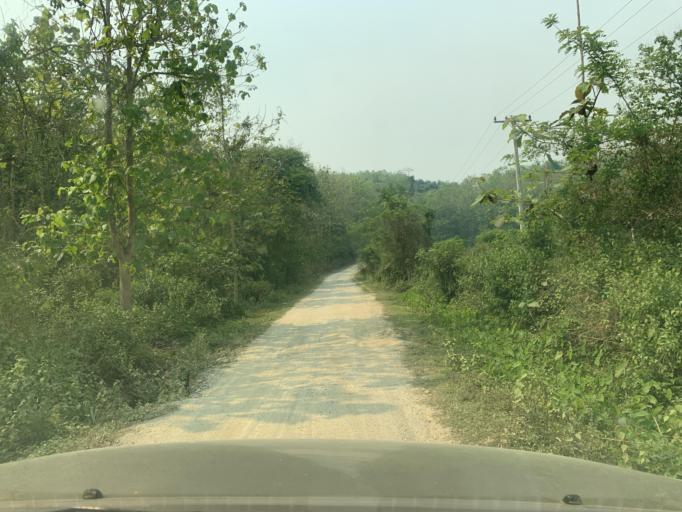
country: LA
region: Louangphabang
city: Louangphabang
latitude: 19.8867
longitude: 102.2523
